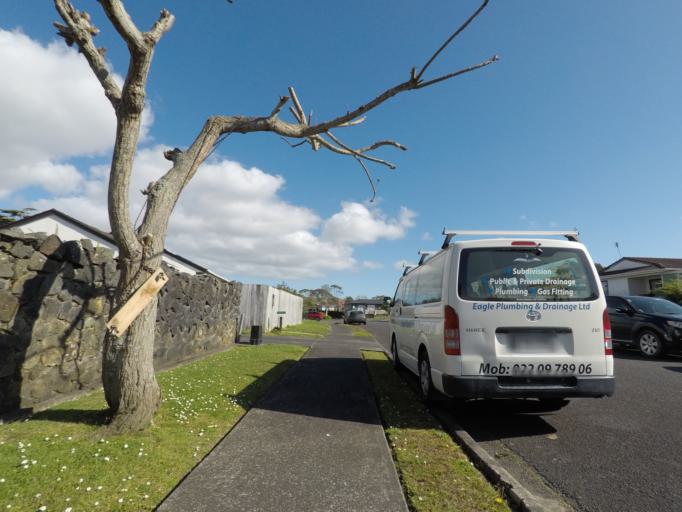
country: NZ
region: Auckland
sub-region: Auckland
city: Rosebank
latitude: -36.8623
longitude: 174.5998
